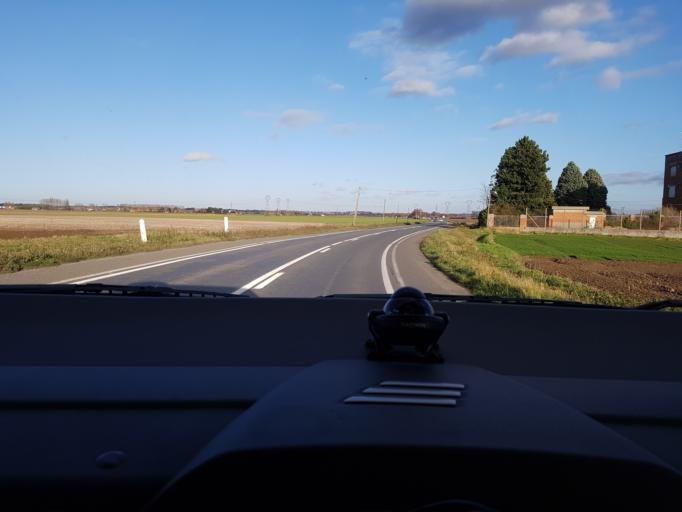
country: FR
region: Nord-Pas-de-Calais
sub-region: Departement du Nord
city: Camphin-en-Carembault
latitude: 50.5195
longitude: 2.9925
